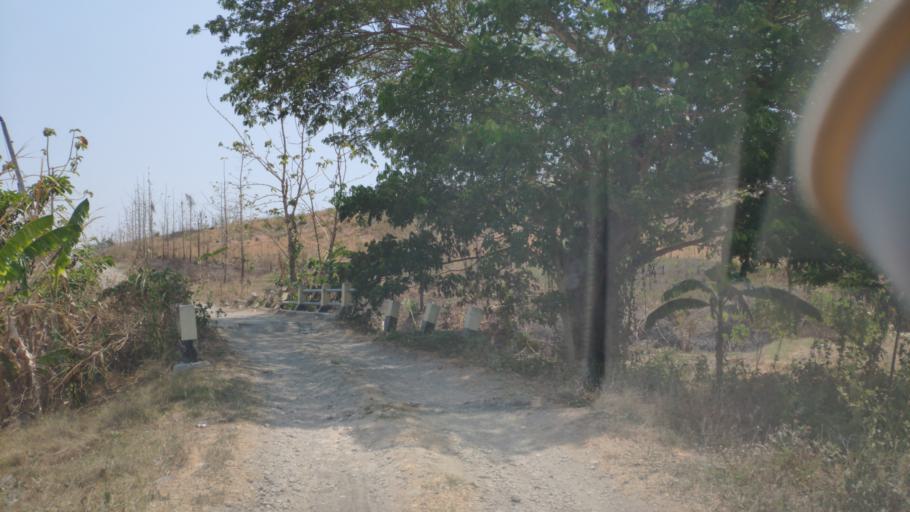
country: ID
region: Central Java
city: Menden
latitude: -7.2986
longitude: 111.4335
